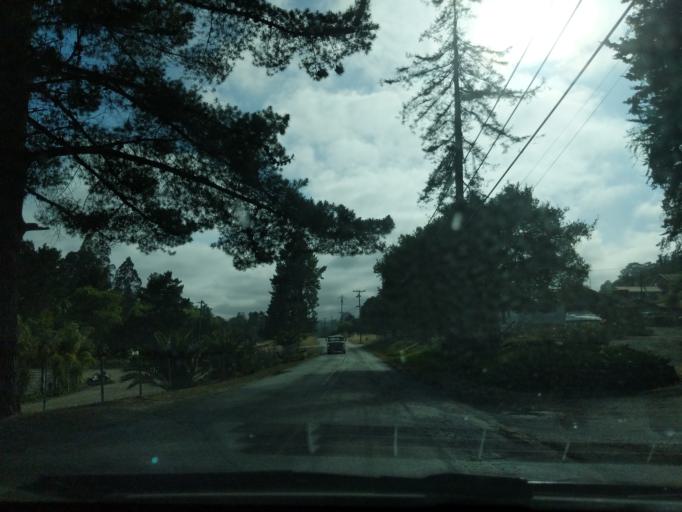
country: US
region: California
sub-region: Monterey County
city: Prunedale
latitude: 36.7978
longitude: -121.6486
